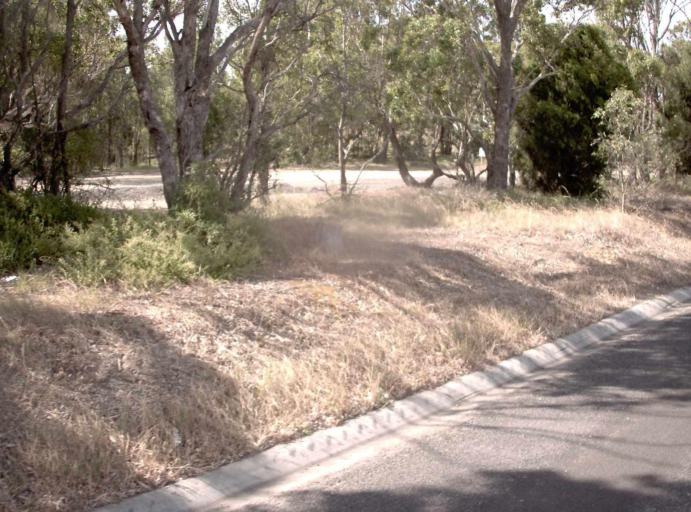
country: AU
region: Victoria
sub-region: East Gippsland
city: Bairnsdale
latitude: -37.8238
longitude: 147.7199
